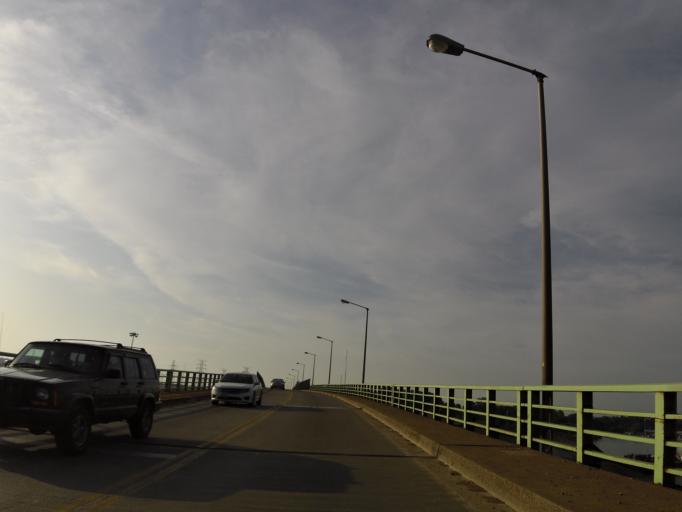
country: US
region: Tennessee
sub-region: Loudon County
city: Lenoir City
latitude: 35.7881
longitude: -84.2410
